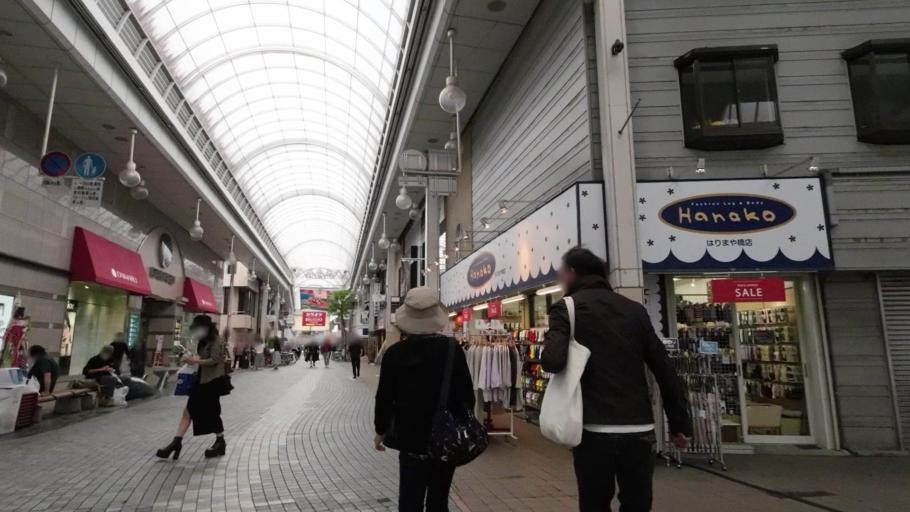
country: JP
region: Kochi
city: Kochi-shi
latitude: 33.5610
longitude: 133.5417
